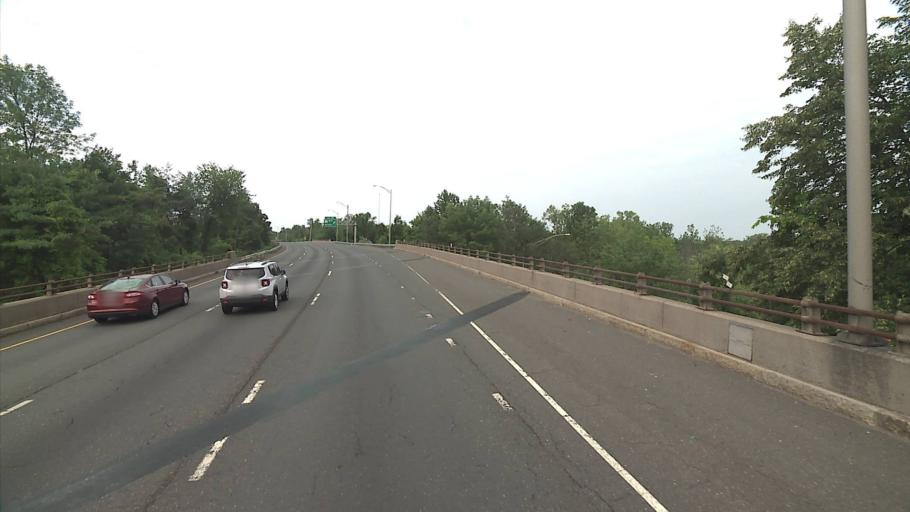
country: US
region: Connecticut
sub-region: Hartford County
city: Farmington
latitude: 41.7224
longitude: -72.7925
